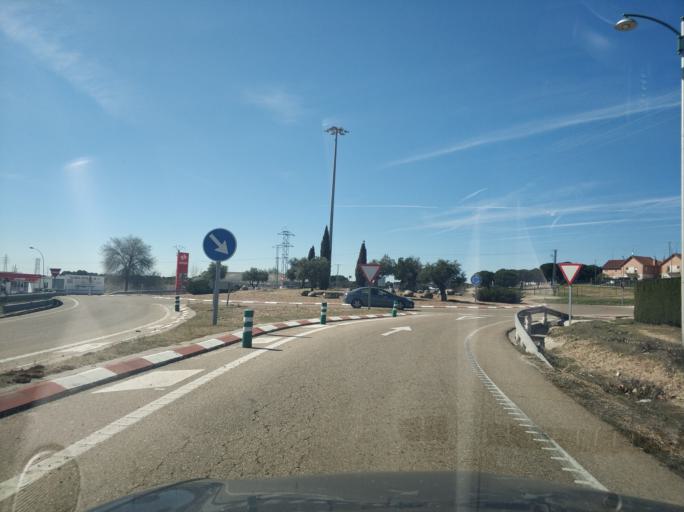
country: ES
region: Castille and Leon
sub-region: Provincia de Valladolid
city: Boecillo
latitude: 41.5375
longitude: -4.6987
